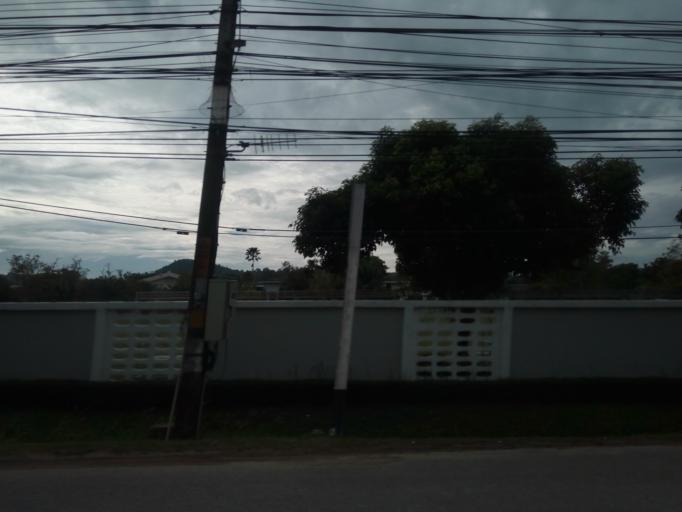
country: TH
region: Phuket
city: Thalang
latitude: 8.0666
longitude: 98.3430
